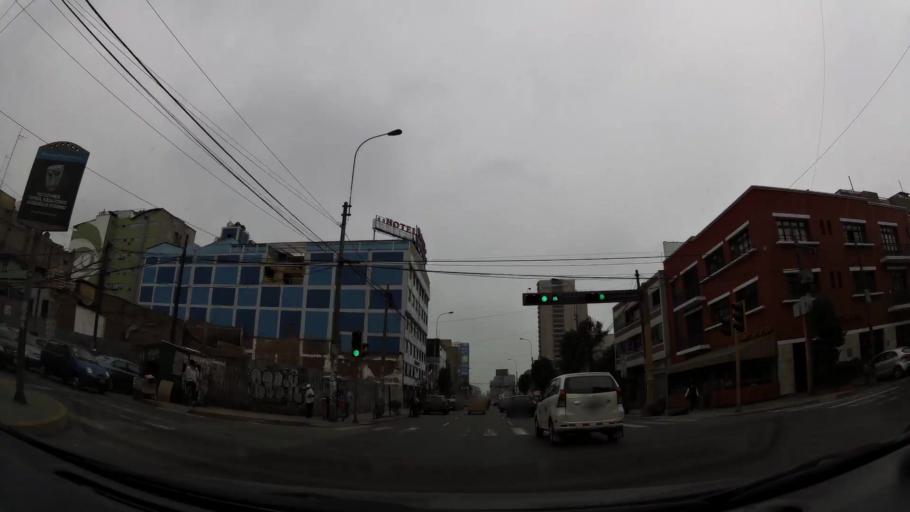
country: PE
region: Lima
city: Lima
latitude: -12.0757
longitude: -77.0369
